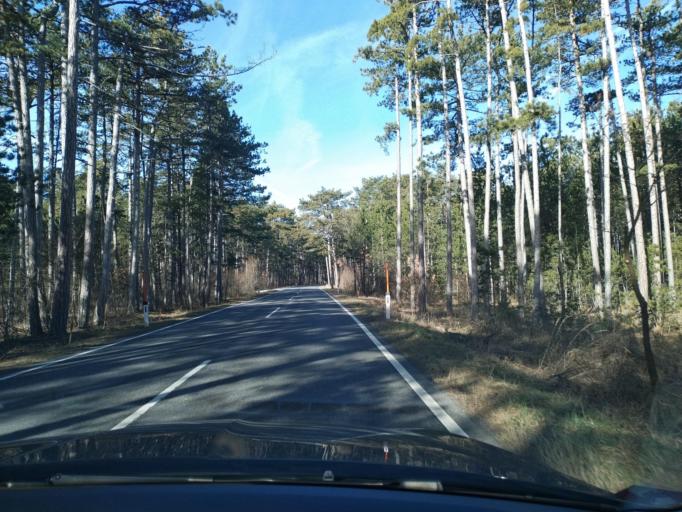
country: AT
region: Lower Austria
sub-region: Politischer Bezirk Neunkirchen
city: Breitenau
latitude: 47.7555
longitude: 16.1569
